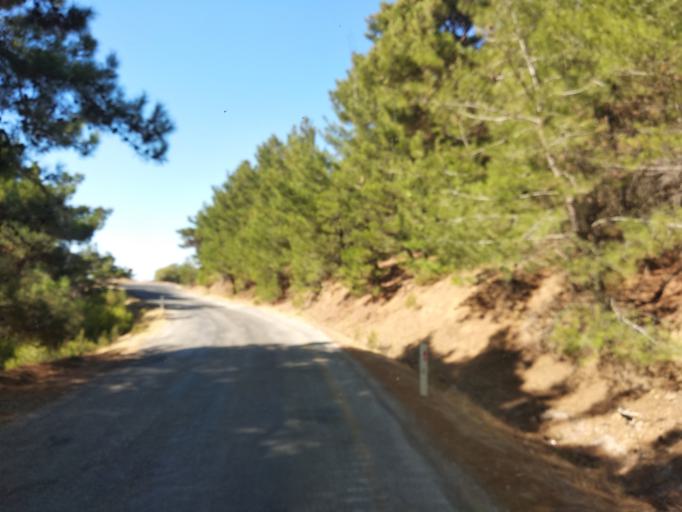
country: TR
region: Izmir
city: Gaziemir
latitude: 38.3024
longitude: 26.9978
